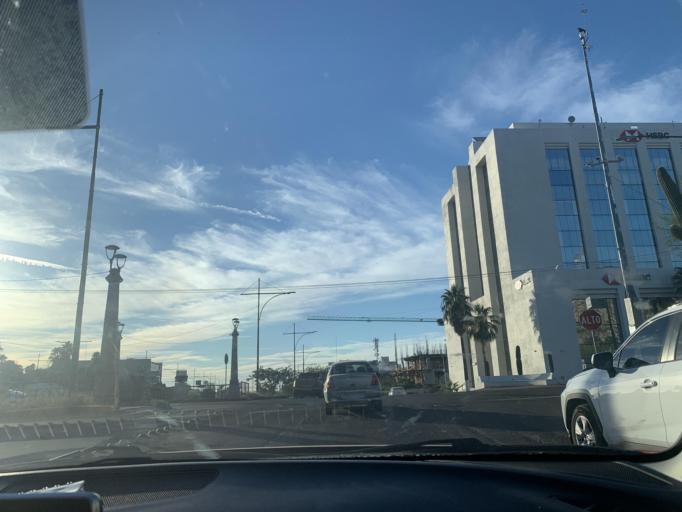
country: MX
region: Sonora
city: Hermosillo
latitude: 29.0692
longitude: -110.9576
